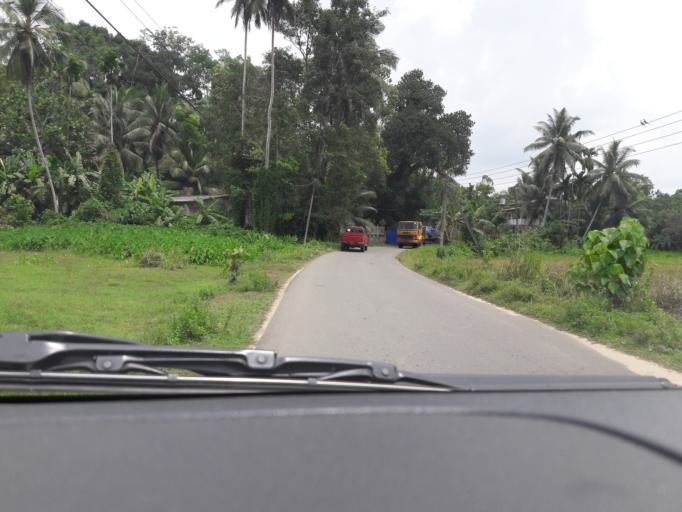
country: LK
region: Southern
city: Galle
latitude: 6.1793
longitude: 80.2899
